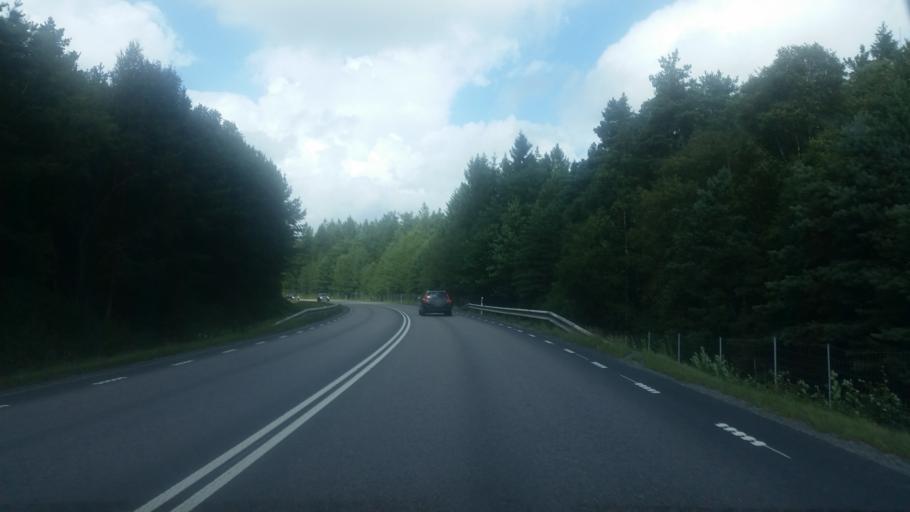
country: SE
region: Vaestra Goetaland
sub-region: Partille Kommun
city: Furulund
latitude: 57.7086
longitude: 12.1516
